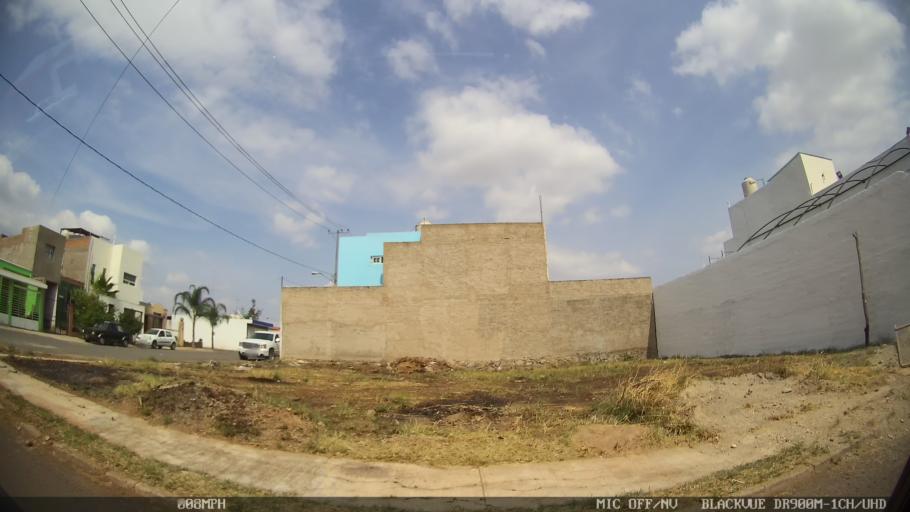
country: MX
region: Jalisco
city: Coyula
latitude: 20.6378
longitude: -103.2163
